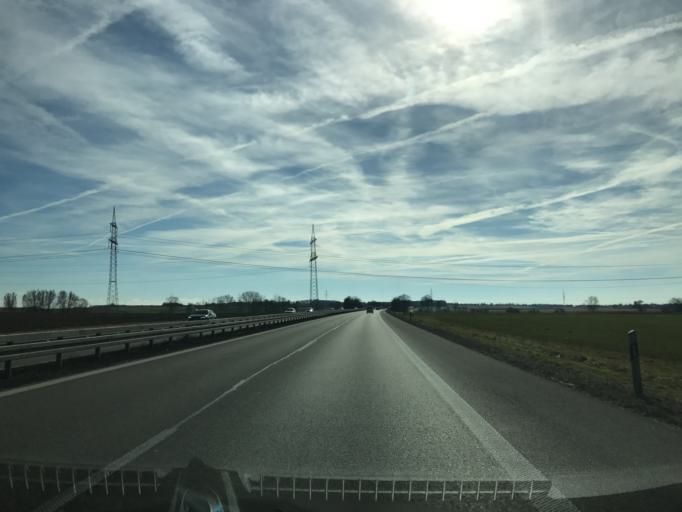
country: DE
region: Baden-Wuerttemberg
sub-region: Tuebingen Region
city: Huttisheim
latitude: 48.2991
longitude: 9.9228
